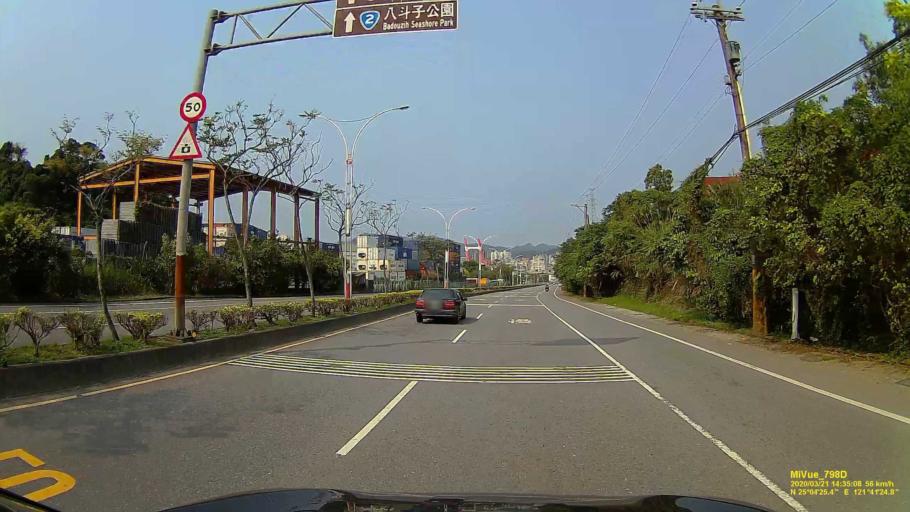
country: TW
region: Taiwan
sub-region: Keelung
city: Keelung
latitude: 25.0740
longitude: 121.6903
